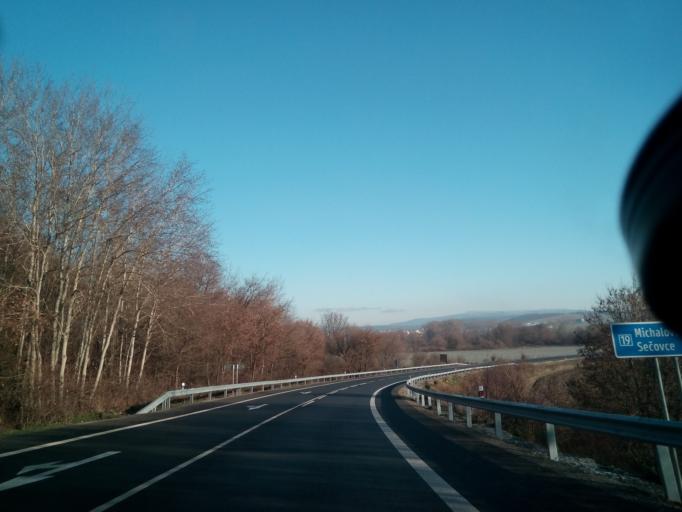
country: SK
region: Kosicky
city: Kosice
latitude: 48.7305
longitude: 21.3278
